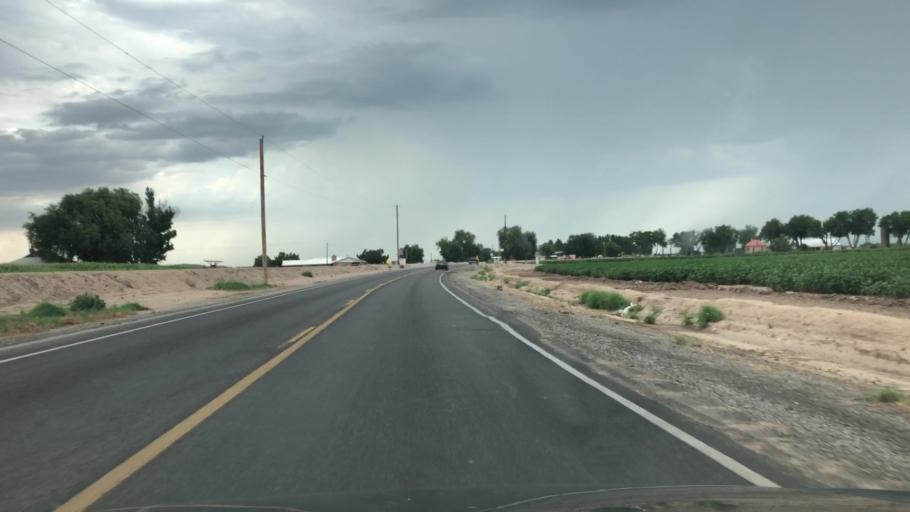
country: US
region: New Mexico
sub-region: Dona Ana County
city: Berino
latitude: 32.0249
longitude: -106.6715
